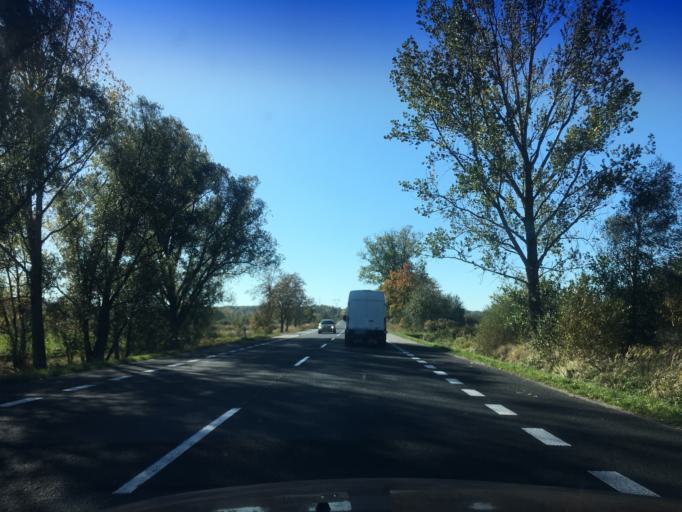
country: DE
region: Saxony
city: Ostritz
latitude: 51.0298
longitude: 14.9694
